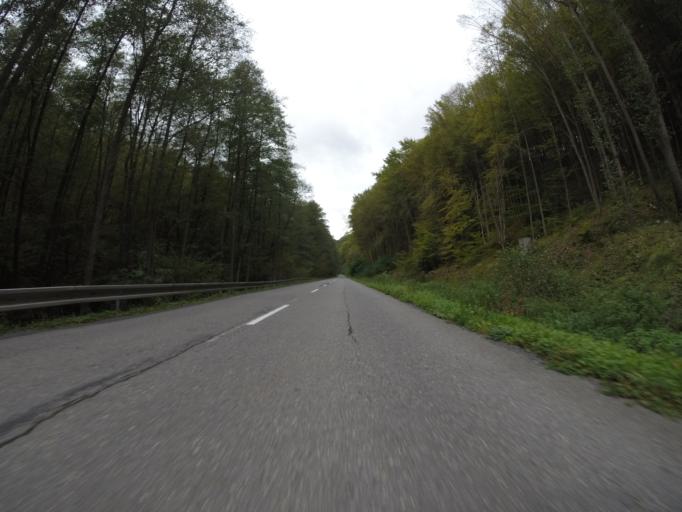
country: SK
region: Banskobystricky
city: Poltar
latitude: 48.5816
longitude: 19.8080
